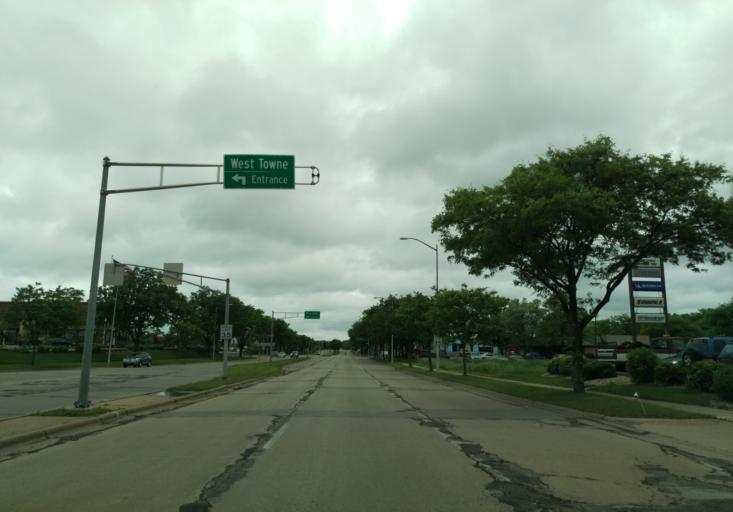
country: US
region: Wisconsin
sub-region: Dane County
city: Middleton
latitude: 43.0571
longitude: -89.5028
